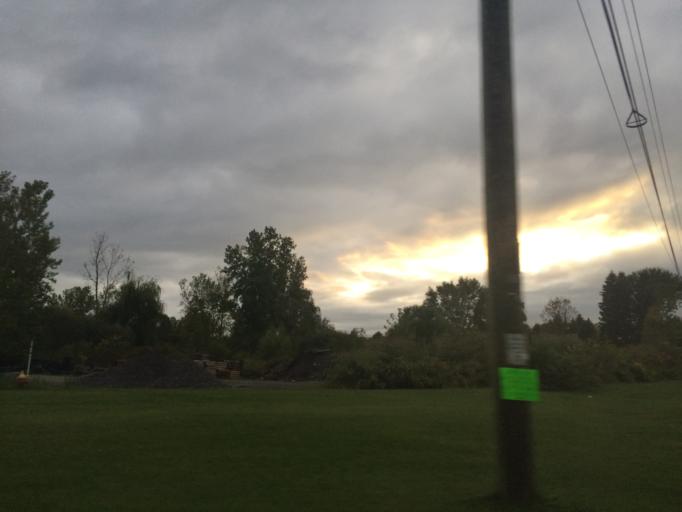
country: US
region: New York
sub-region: Erie County
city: Billington Heights
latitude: 42.8049
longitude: -78.6223
